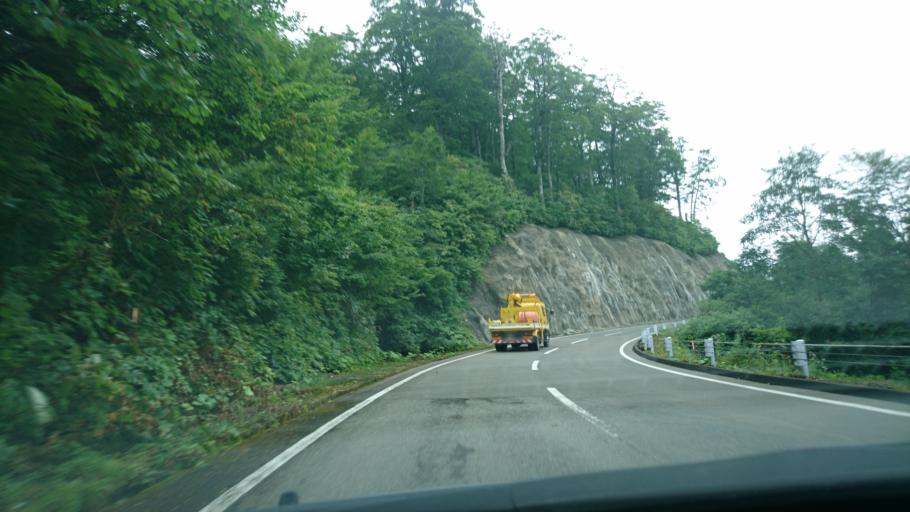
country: JP
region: Akita
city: Yuzawa
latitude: 38.9828
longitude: 140.7353
